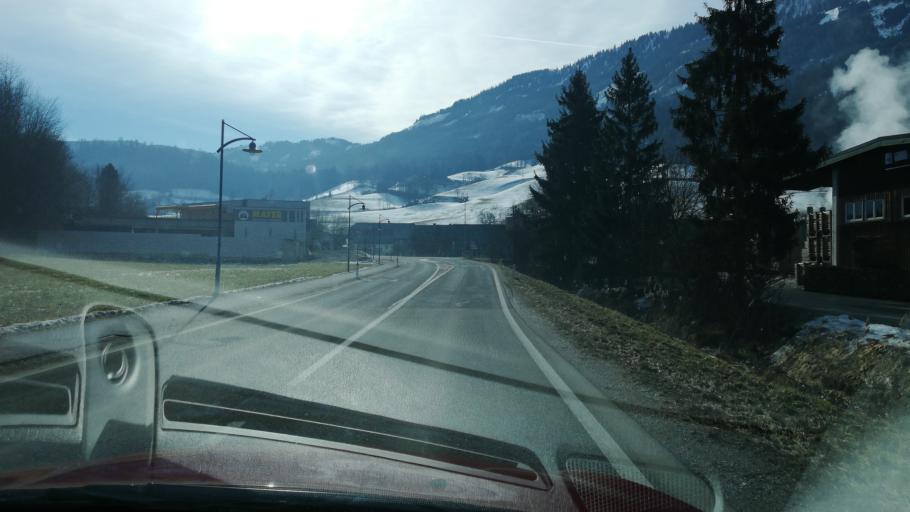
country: AT
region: Styria
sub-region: Politischer Bezirk Liezen
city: Weissenbach bei Liezen
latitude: 47.5466
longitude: 14.2069
